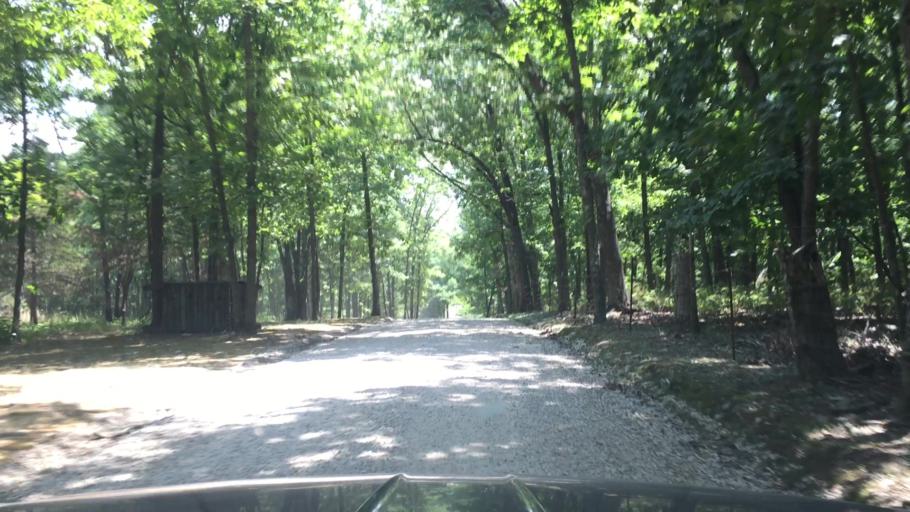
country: US
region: Missouri
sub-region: Miller County
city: Tuscumbia
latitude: 38.1310
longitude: -92.4416
